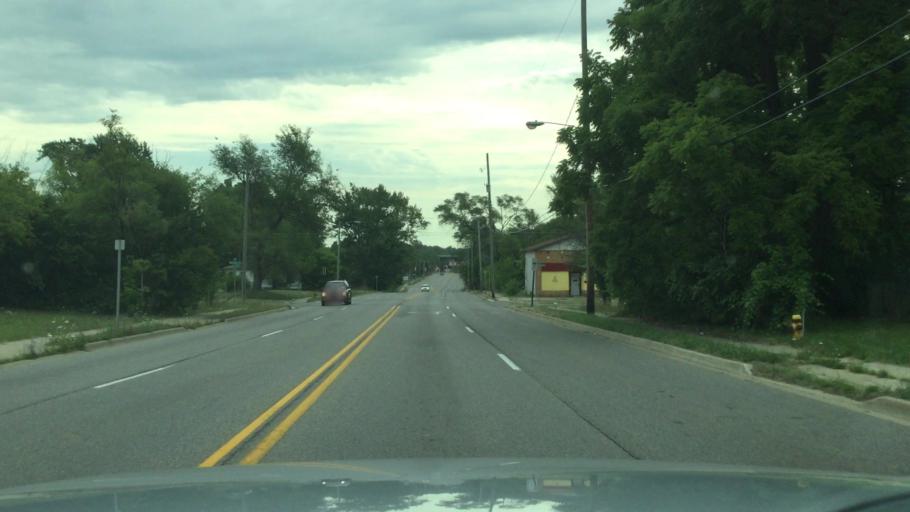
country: US
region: Michigan
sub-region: Genesee County
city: Beecher
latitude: 43.0612
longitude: -83.6884
